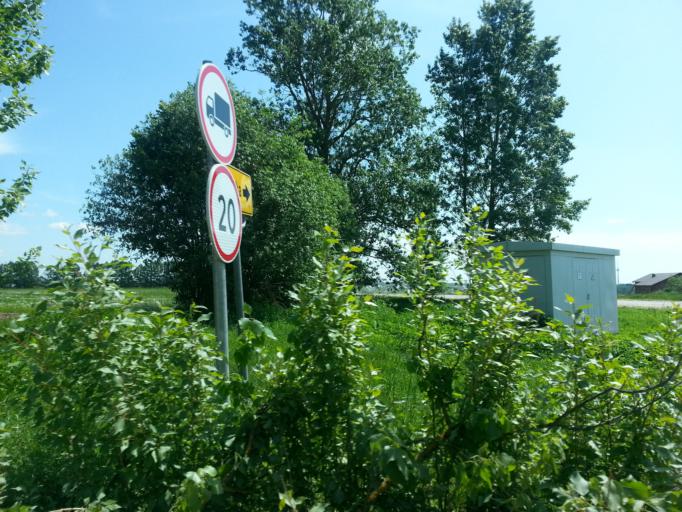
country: LT
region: Vilnius County
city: Pilaite
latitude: 54.7328
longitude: 25.1553
